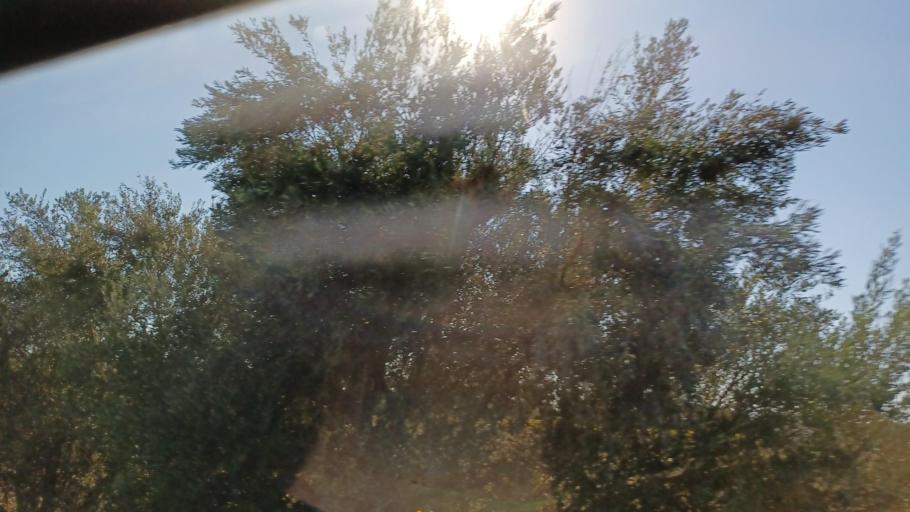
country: CY
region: Larnaka
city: Kolossi
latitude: 34.6596
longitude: 32.9369
